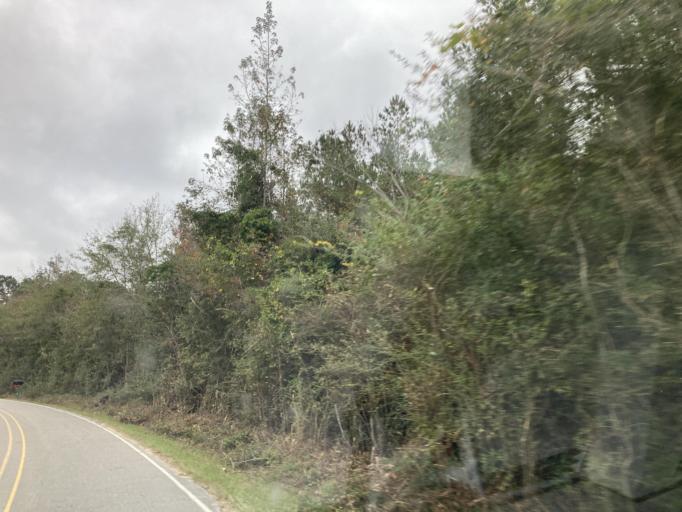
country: US
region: Mississippi
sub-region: Lamar County
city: Purvis
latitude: 31.1776
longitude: -89.4190
